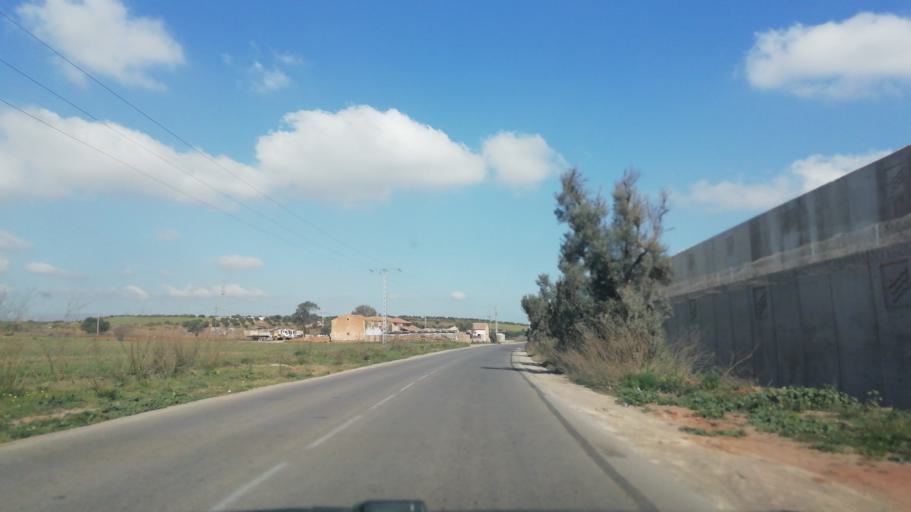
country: DZ
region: Oran
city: Ain el Bya
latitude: 35.7593
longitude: -0.2751
